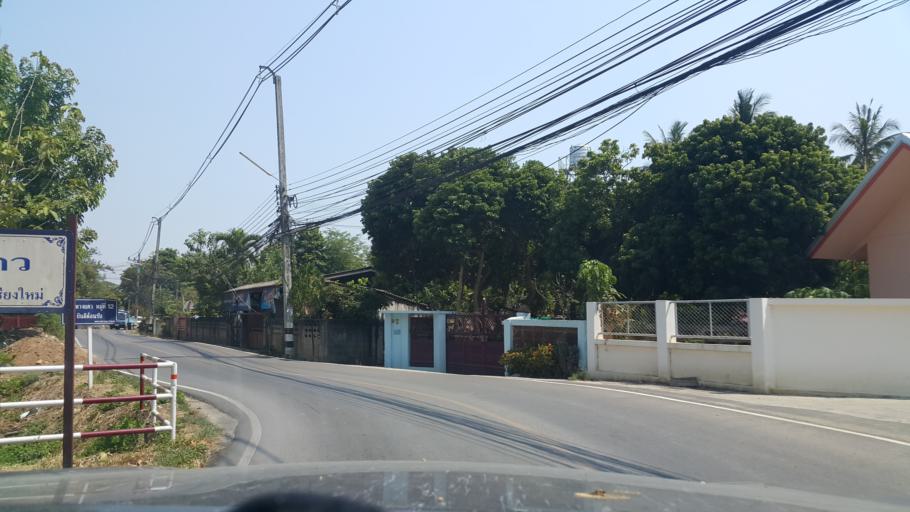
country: TH
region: Chiang Mai
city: Saraphi
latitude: 18.7270
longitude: 98.9887
